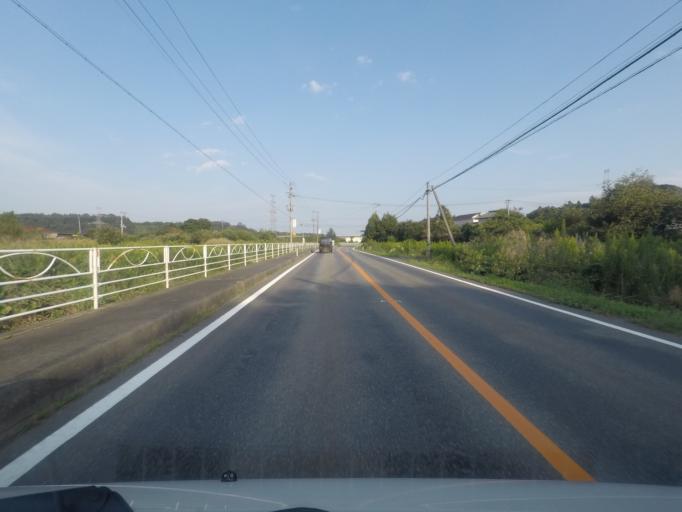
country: JP
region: Fukushima
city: Namie
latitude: 37.5066
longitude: 140.9374
